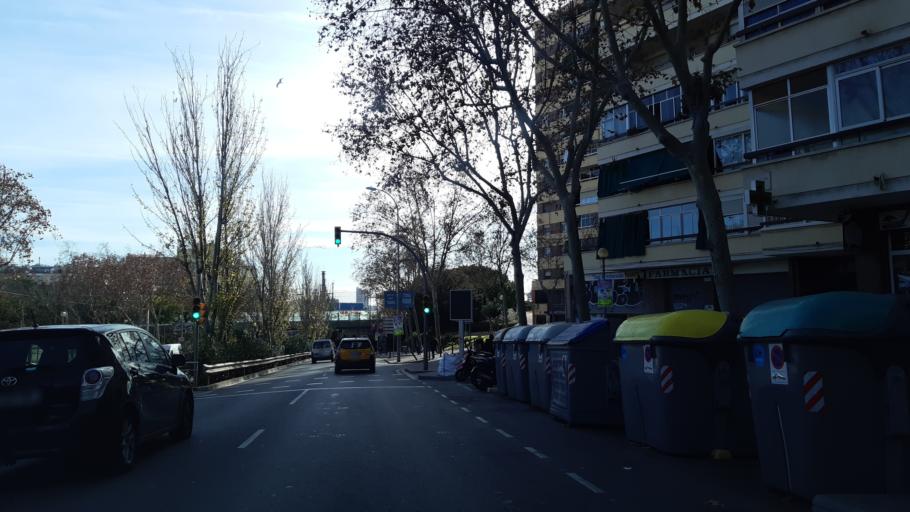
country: ES
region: Catalonia
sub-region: Provincia de Barcelona
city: L'Hospitalet de Llobregat
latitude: 41.3664
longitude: 2.1038
